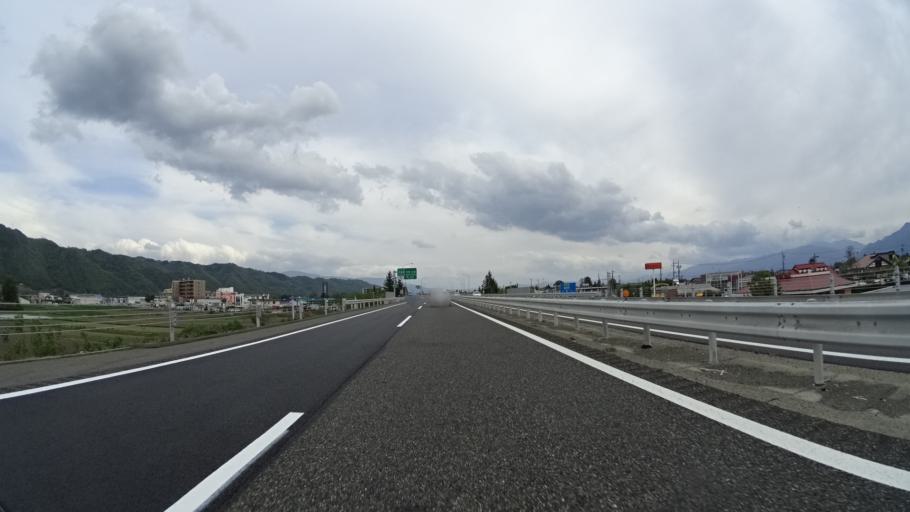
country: JP
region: Nagano
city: Toyoshina
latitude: 36.3023
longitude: 137.9237
